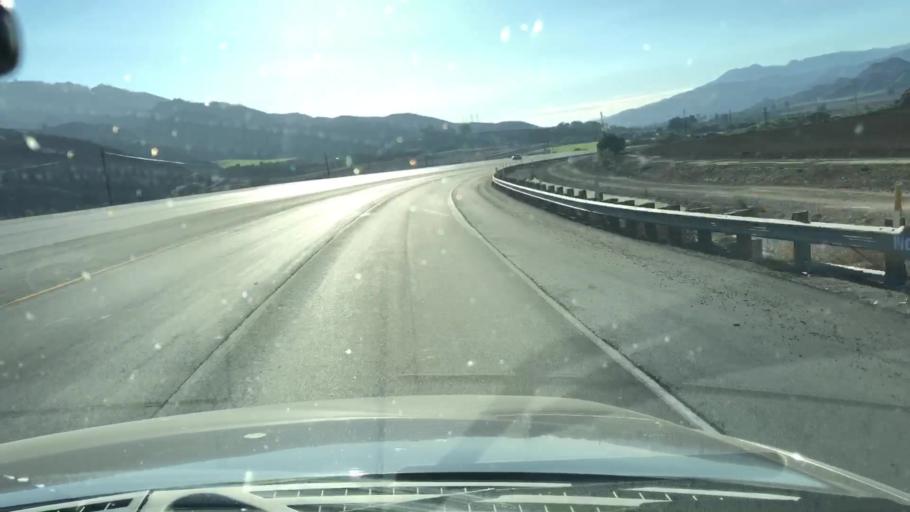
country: US
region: California
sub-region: Los Angeles County
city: Val Verde
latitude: 34.4029
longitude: -118.7065
